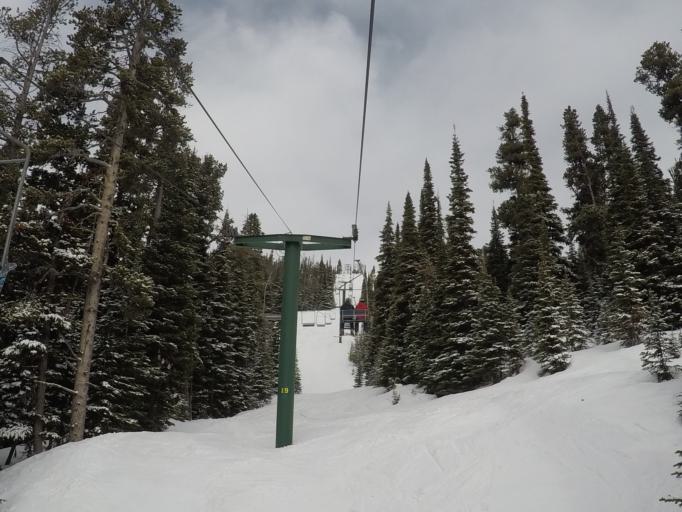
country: US
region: Montana
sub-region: Meagher County
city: White Sulphur Springs
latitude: 46.8348
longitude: -110.7115
